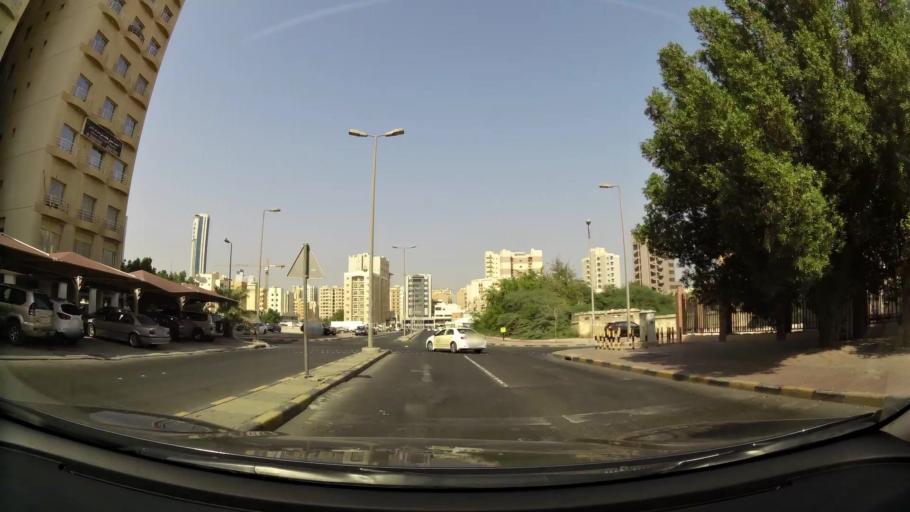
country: KW
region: Muhafazat Hawalli
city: Hawalli
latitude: 29.3445
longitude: 48.0202
